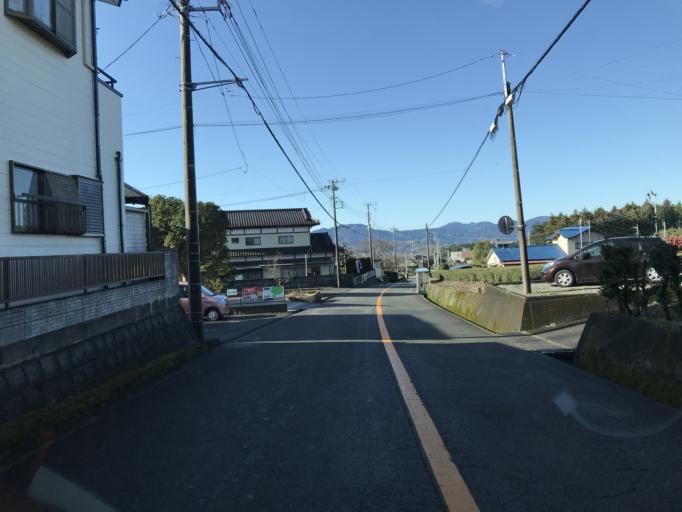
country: JP
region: Shizuoka
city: Fujinomiya
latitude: 35.2282
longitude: 138.6493
